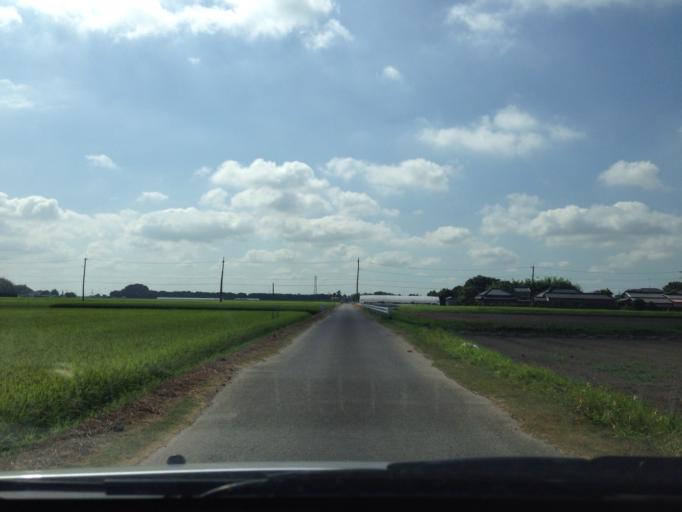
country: JP
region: Ibaraki
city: Inashiki
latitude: 36.0128
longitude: 140.3640
